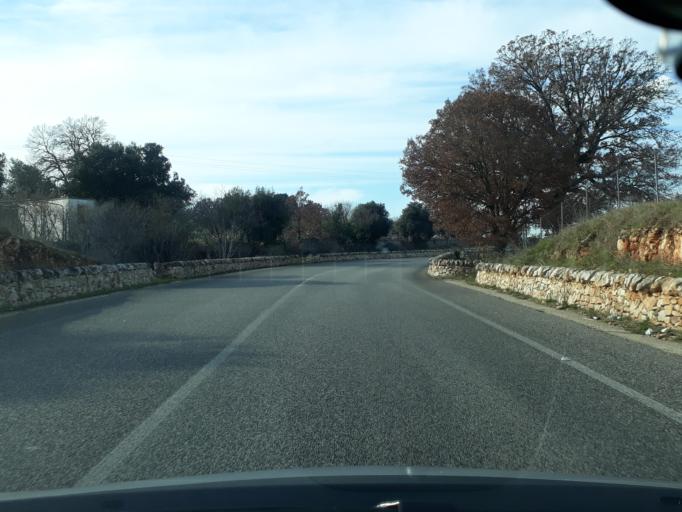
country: IT
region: Apulia
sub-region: Provincia di Bari
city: Locorotondo
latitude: 40.7606
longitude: 17.3358
